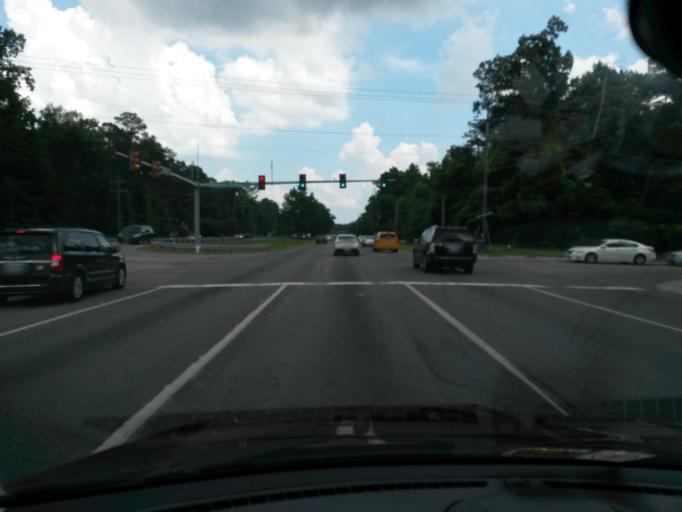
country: US
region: Virginia
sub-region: Chesterfield County
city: Enon
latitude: 37.3474
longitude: -77.3505
